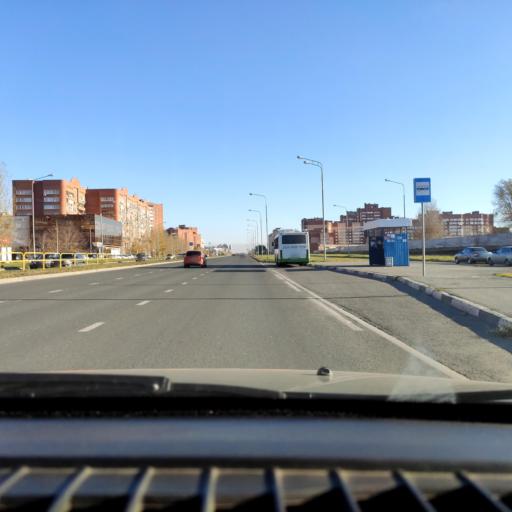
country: RU
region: Samara
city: Tol'yatti
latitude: 53.5338
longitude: 49.3474
